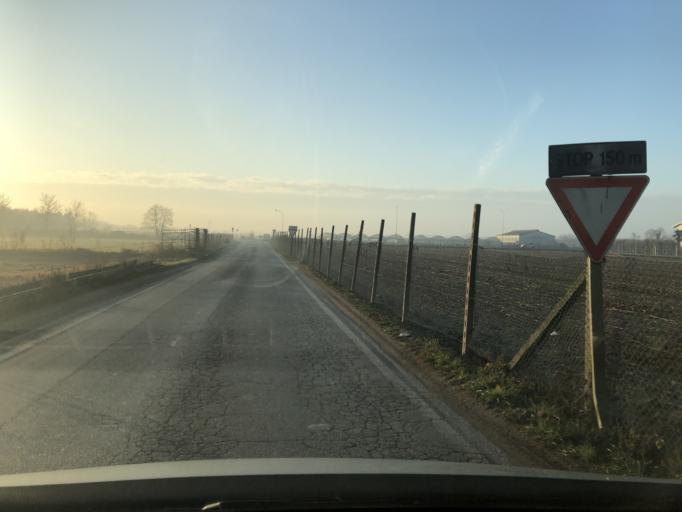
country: IT
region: Veneto
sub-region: Provincia di Verona
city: Caselle
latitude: 45.4103
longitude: 10.8771
